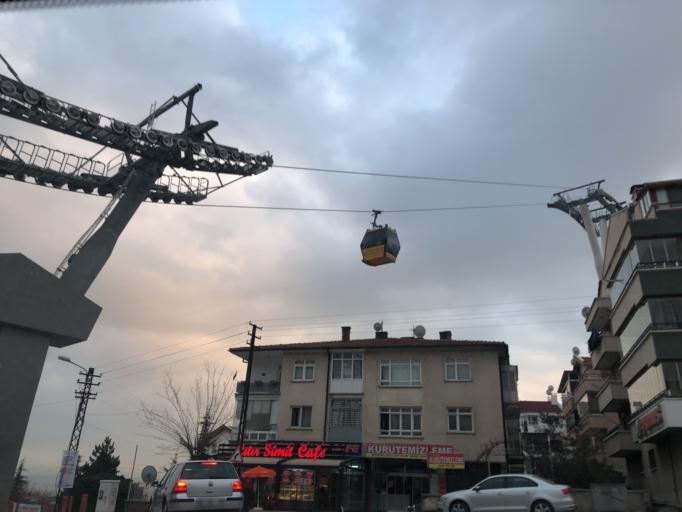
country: TR
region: Ankara
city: Ankara
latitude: 39.9696
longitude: 32.8080
